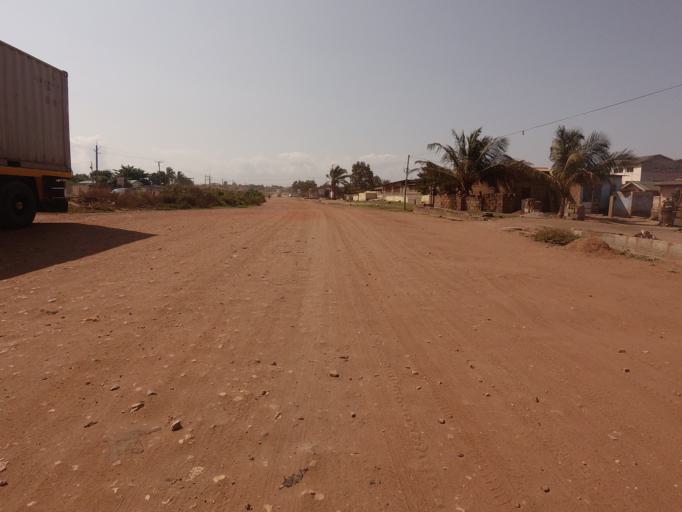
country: GH
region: Greater Accra
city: Teshi Old Town
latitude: 5.5871
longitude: -0.1148
